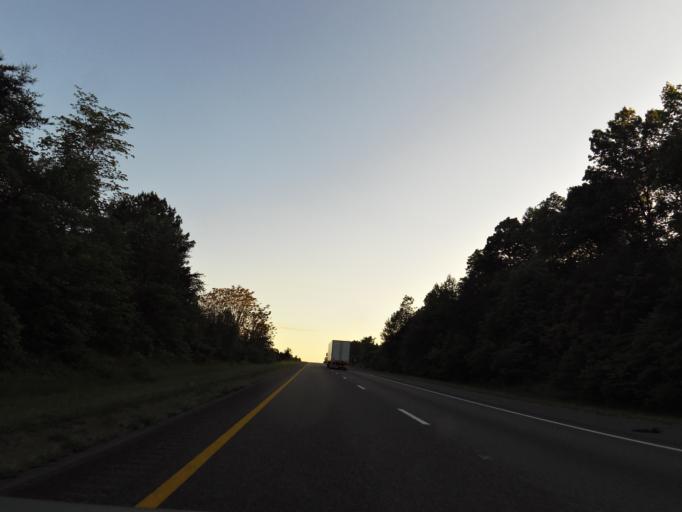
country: US
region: Tennessee
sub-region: Washington County
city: Fall Branch
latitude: 36.3960
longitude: -82.6529
